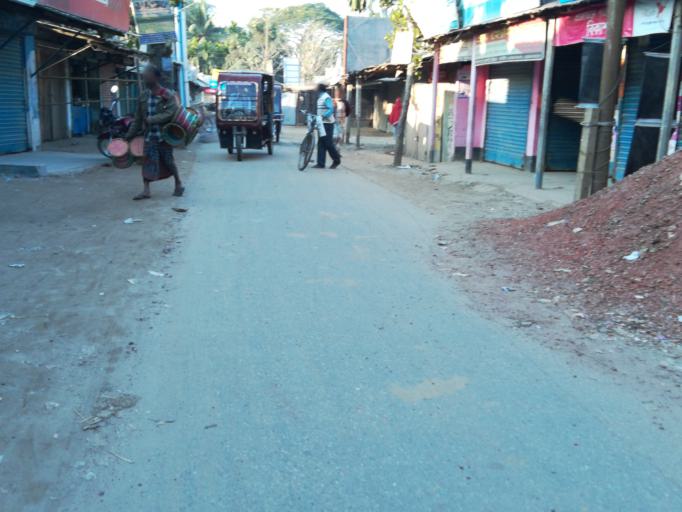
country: BD
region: Rangpur Division
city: Lalmanirhat
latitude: 25.9474
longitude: 89.5523
